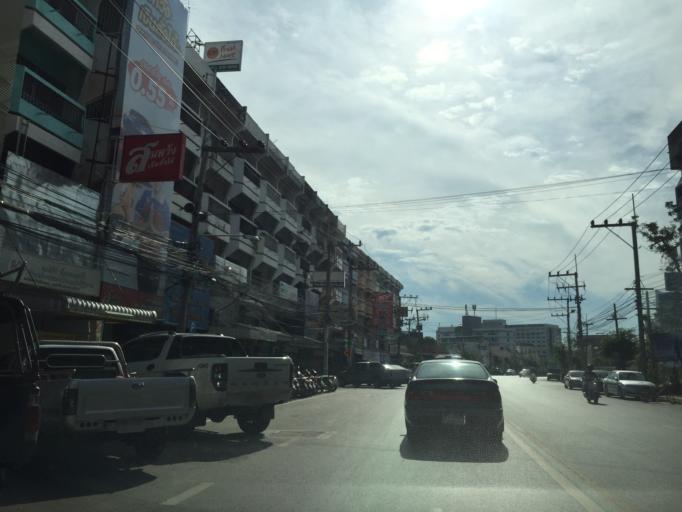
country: TH
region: Phitsanulok
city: Phitsanulok
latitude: 16.8200
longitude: 100.2701
